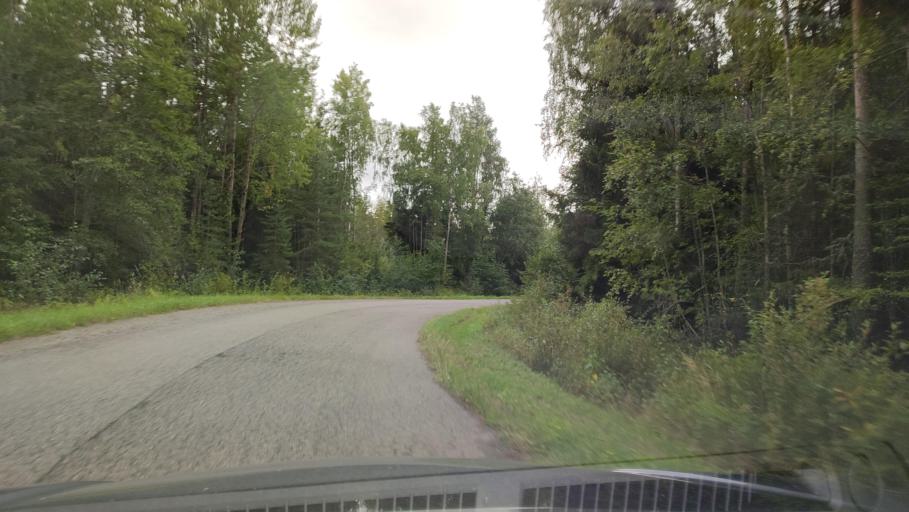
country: FI
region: Ostrobothnia
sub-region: Sydosterbotten
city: Kristinestad
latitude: 62.2543
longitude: 21.3356
